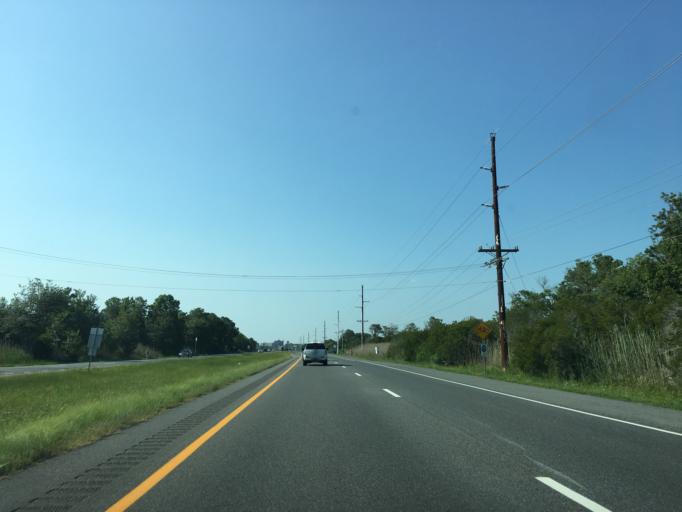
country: US
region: Delaware
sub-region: Sussex County
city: Bethany Beach
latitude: 38.5551
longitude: -75.0600
